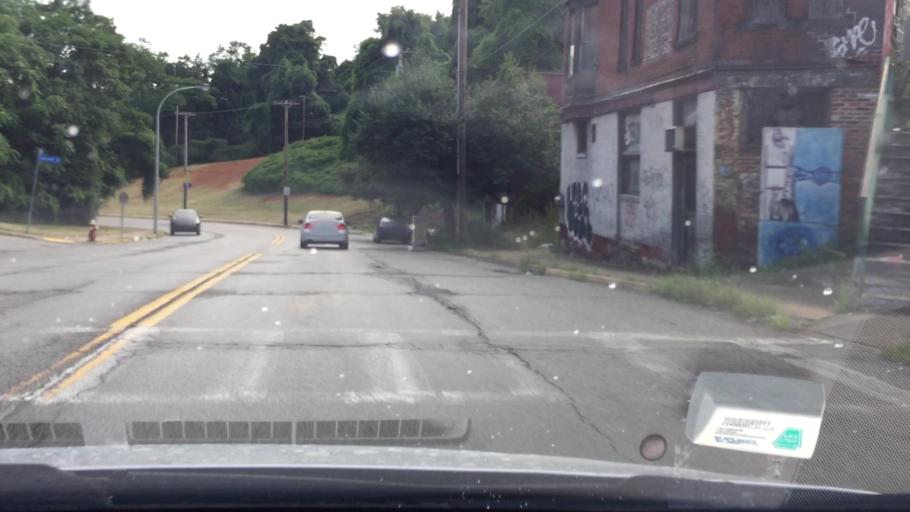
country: US
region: Pennsylvania
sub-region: Allegheny County
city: Bloomfield
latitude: 40.4508
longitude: -79.9651
